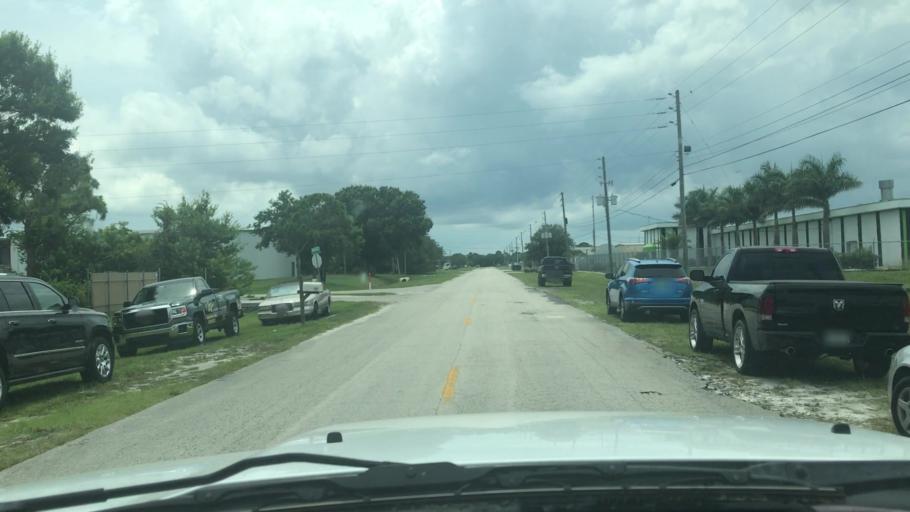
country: US
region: Florida
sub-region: Saint Lucie County
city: Fort Pierce North
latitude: 27.4937
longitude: -80.3511
